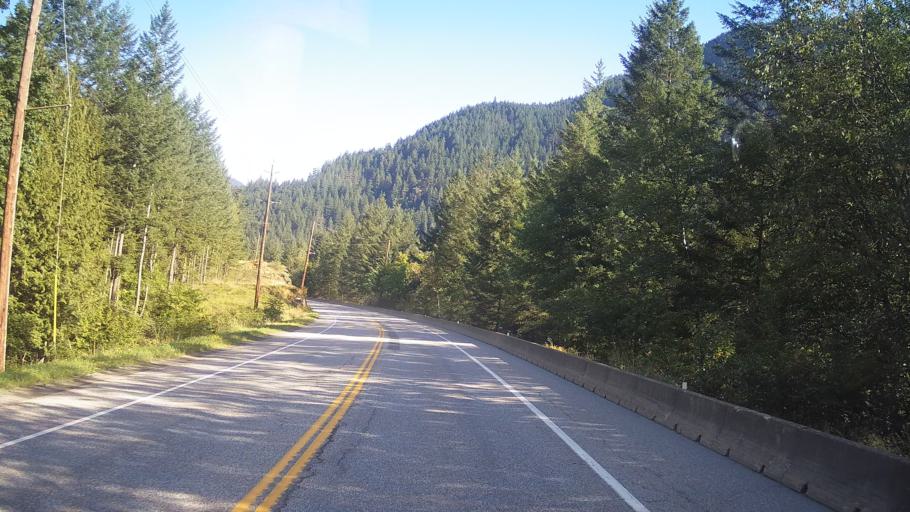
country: CA
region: British Columbia
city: Hope
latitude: 49.6299
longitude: -121.3930
